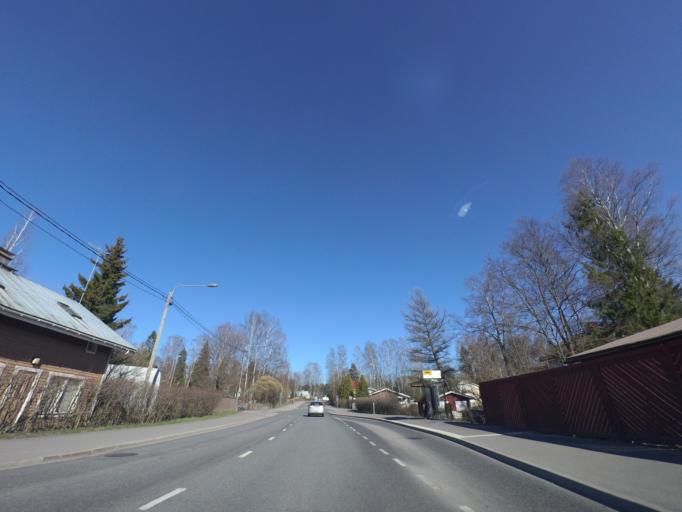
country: FI
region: Uusimaa
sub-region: Helsinki
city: Vantaa
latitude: 60.2500
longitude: 25.0957
